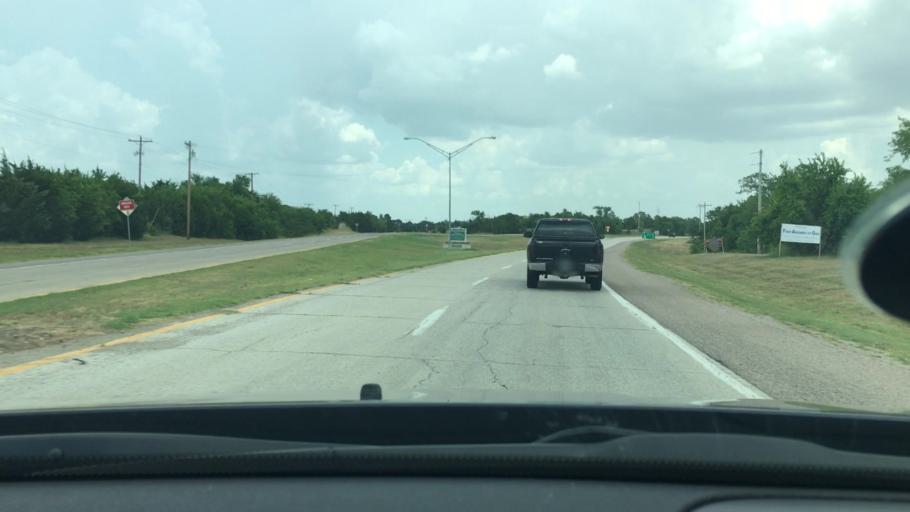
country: US
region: Oklahoma
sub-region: Marshall County
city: Madill
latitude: 34.0770
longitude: -96.7843
